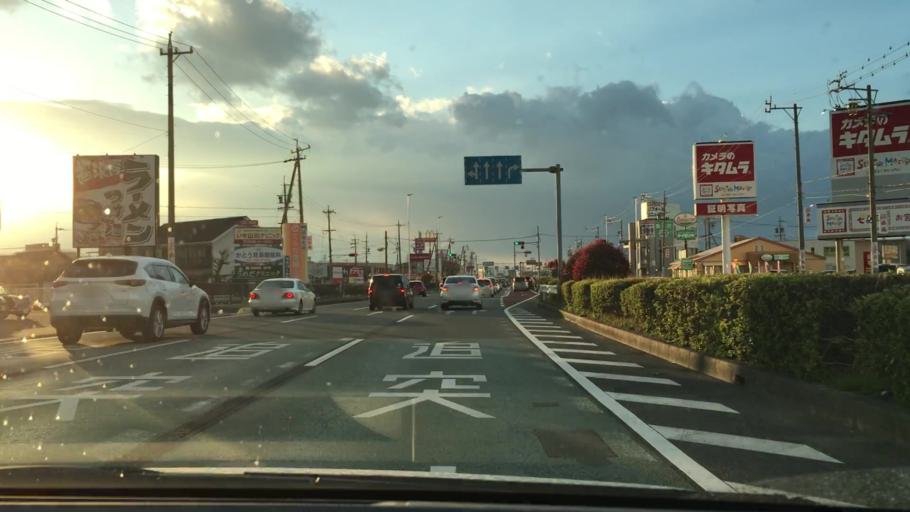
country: JP
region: Mie
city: Ise
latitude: 34.5064
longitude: 136.7269
